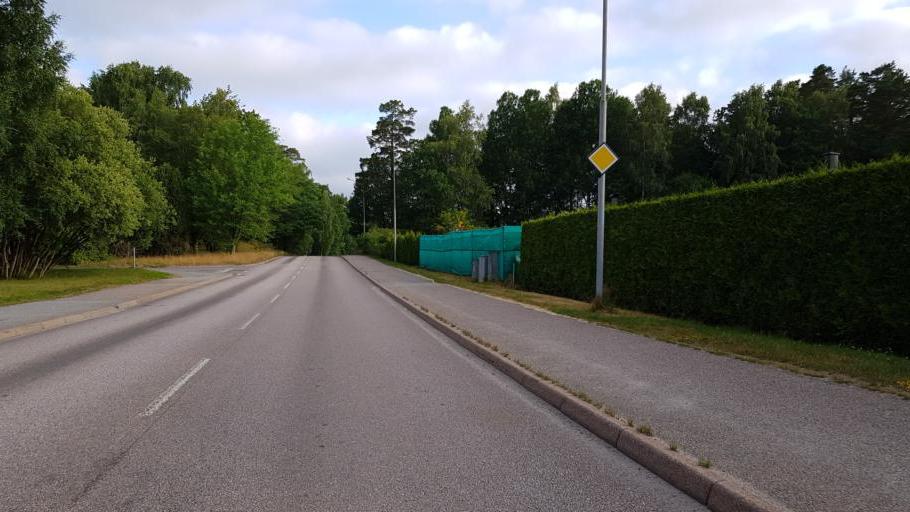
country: SE
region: Vaestra Goetaland
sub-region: Harryda Kommun
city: Molnlycke
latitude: 57.6494
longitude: 12.1124
